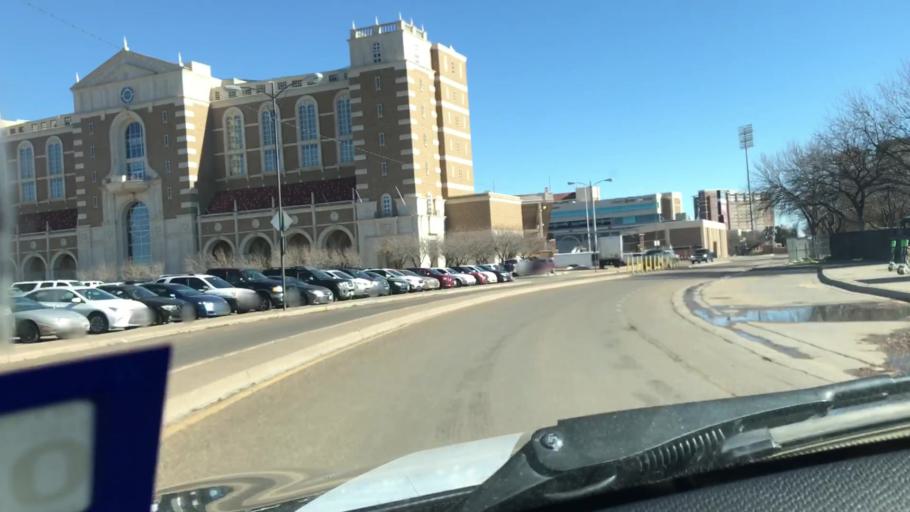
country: US
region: Texas
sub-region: Lubbock County
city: Lubbock
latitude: 33.5900
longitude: -101.8757
